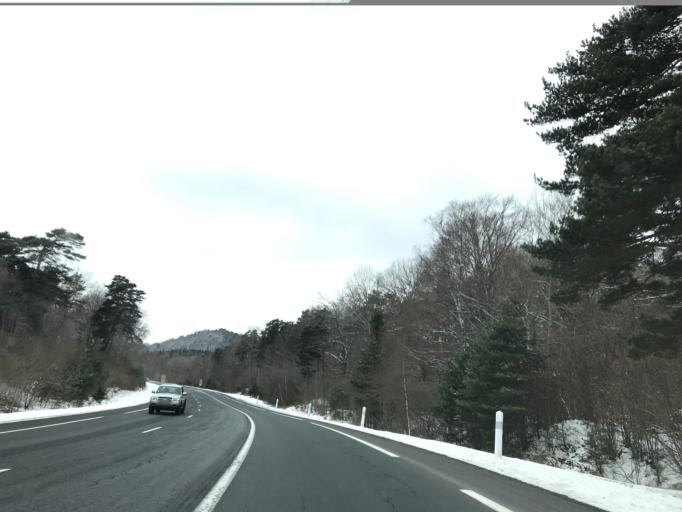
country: FR
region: Auvergne
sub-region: Departement du Puy-de-Dome
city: Aydat
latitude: 45.6912
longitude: 2.9861
